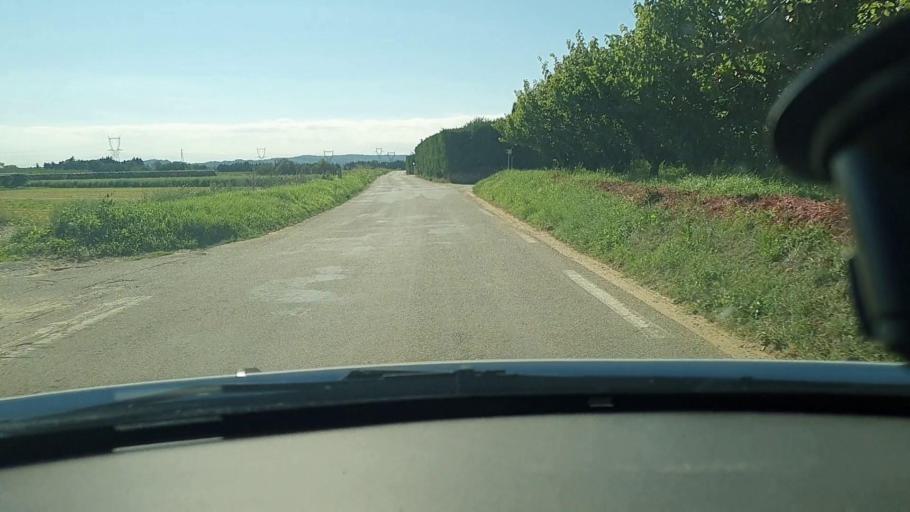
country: FR
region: Languedoc-Roussillon
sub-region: Departement du Gard
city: Saint-Julien-de-Peyrolas
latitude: 44.2884
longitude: 4.5706
